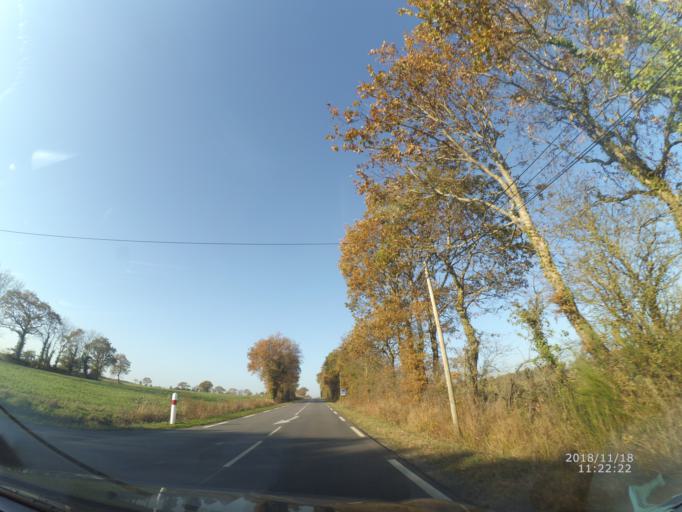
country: FR
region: Pays de la Loire
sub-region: Departement de la Loire-Atlantique
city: Saint-Pere-en-Retz
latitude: 47.2221
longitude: -2.0762
